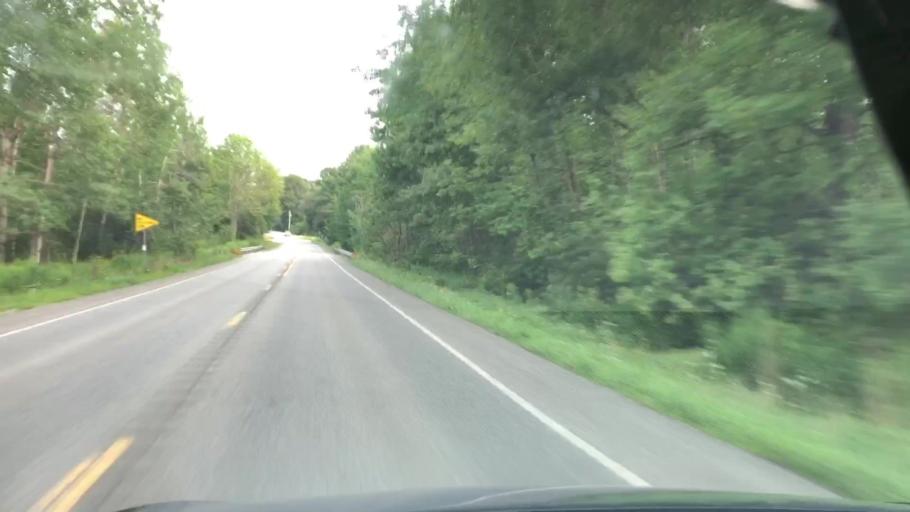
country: US
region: Pennsylvania
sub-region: Erie County
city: Union City
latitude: 41.8363
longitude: -79.8193
